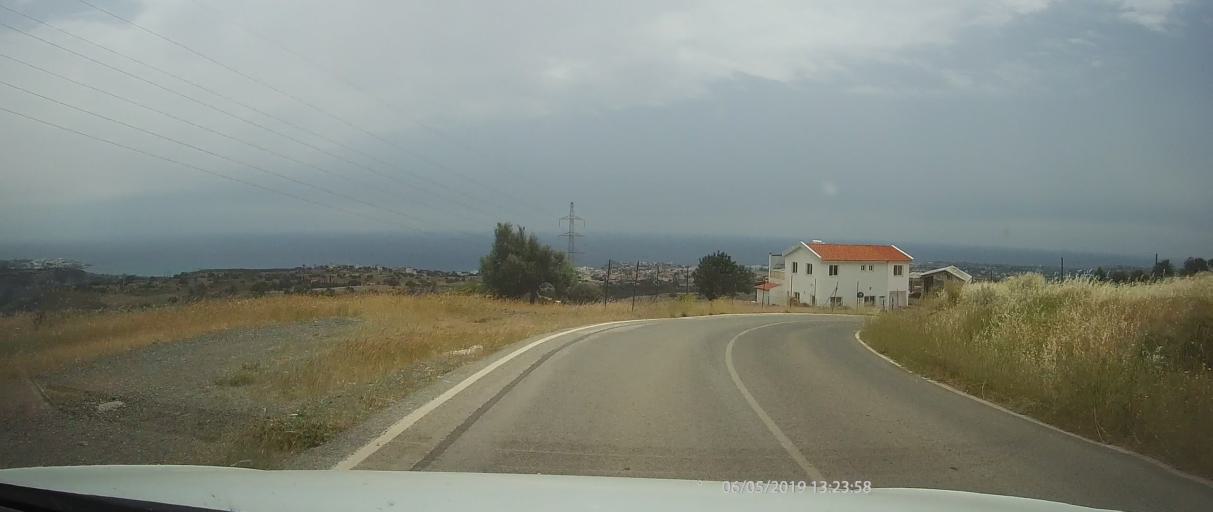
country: CY
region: Pafos
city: Pegeia
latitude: 34.8610
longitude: 32.4015
